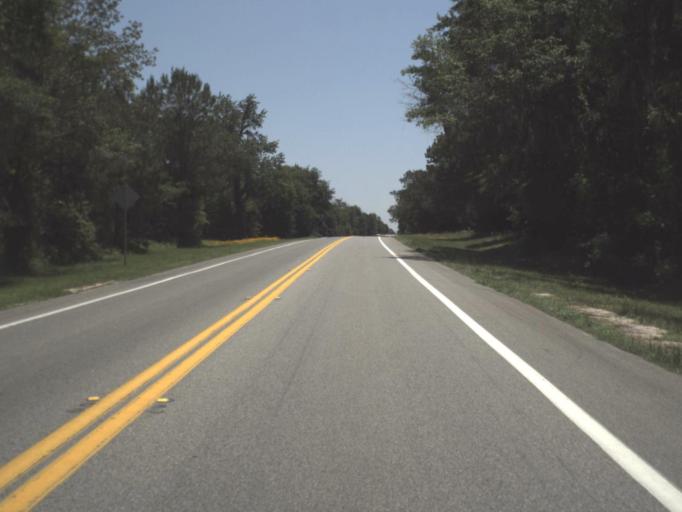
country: US
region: Florida
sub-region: Suwannee County
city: Live Oak
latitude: 30.3310
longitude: -83.0626
